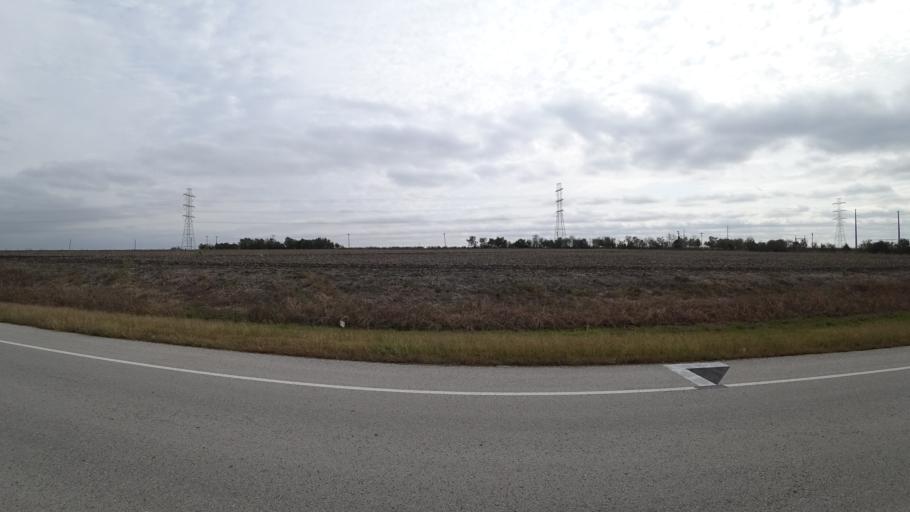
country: US
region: Texas
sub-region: Travis County
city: Manor
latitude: 30.3742
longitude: -97.5817
